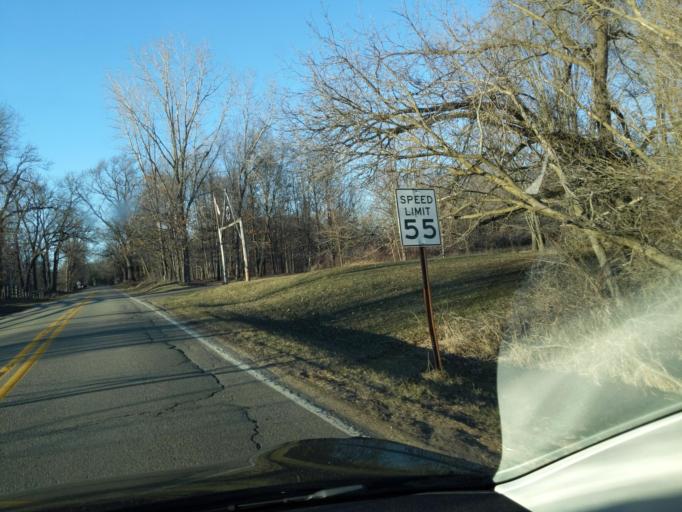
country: US
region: Michigan
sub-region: Livingston County
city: Pinckney
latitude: 42.4317
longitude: -84.0580
